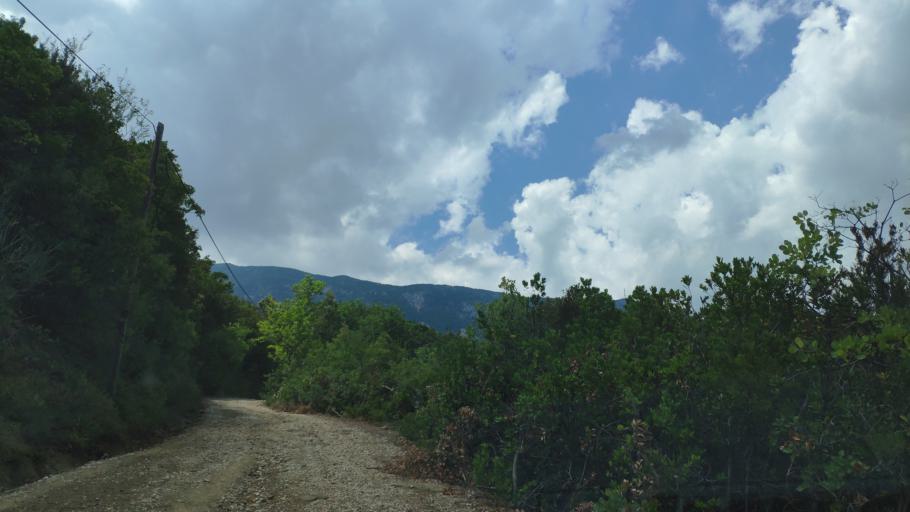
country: GR
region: Epirus
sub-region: Nomos Artas
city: Agios Dimitrios
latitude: 39.3163
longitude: 21.0129
